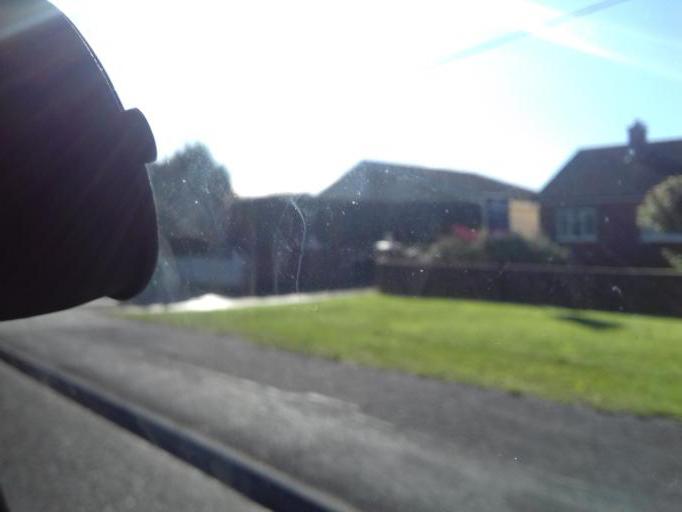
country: IE
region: Leinster
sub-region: Uibh Fhaili
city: Tullamore
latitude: 53.2889
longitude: -7.4995
